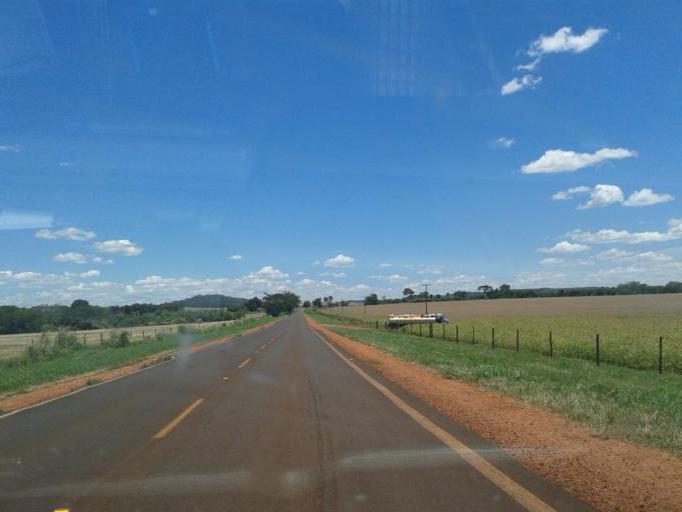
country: BR
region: Minas Gerais
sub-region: Capinopolis
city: Capinopolis
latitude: -18.5836
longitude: -49.5124
